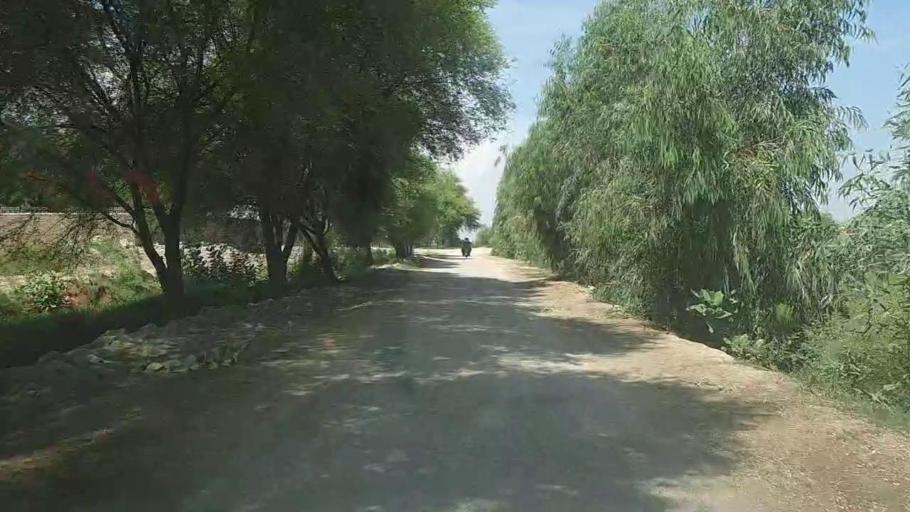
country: PK
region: Sindh
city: Kandhkot
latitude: 28.3003
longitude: 69.2360
